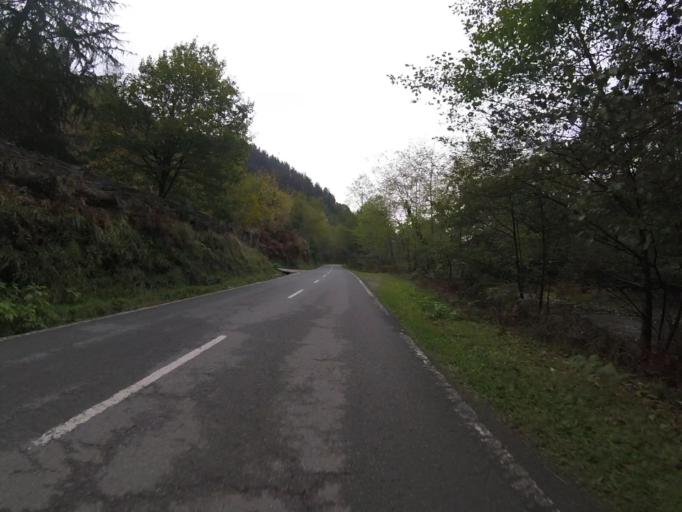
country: ES
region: Navarre
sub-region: Provincia de Navarra
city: Goizueta
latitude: 43.1881
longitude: -1.8572
